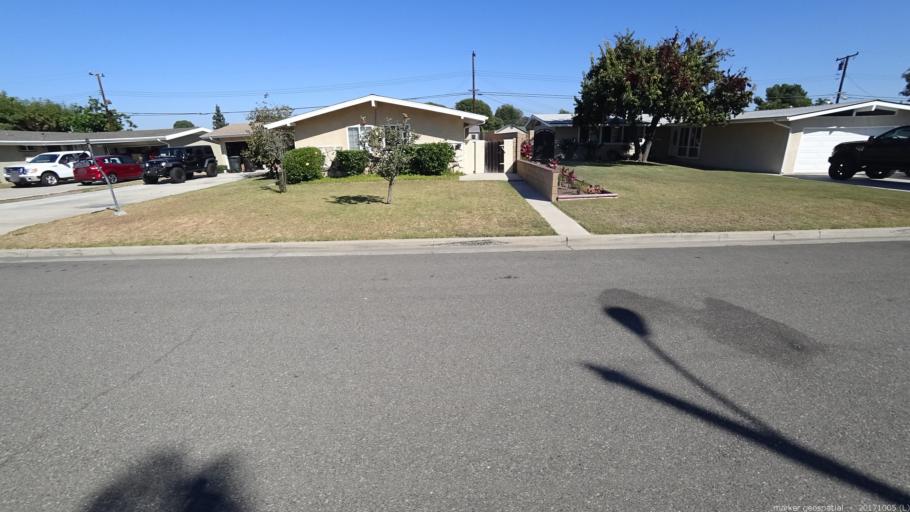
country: US
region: California
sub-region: Orange County
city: Garden Grove
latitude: 33.7841
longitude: -117.9482
